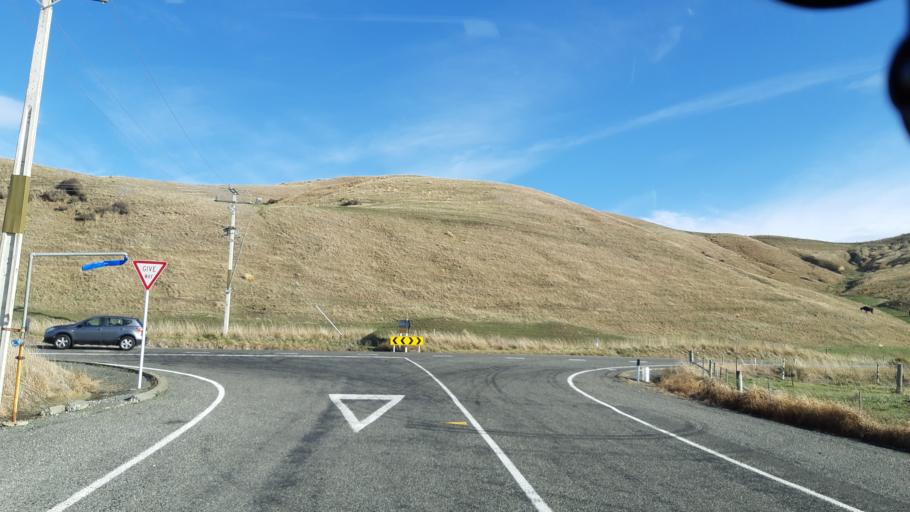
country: NZ
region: Marlborough
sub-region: Marlborough District
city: Blenheim
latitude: -41.7470
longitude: 174.1378
